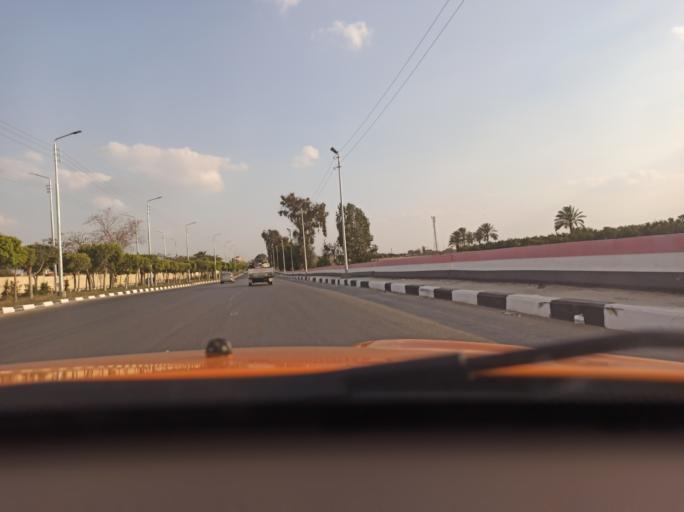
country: EG
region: Al Isma'iliyah
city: Ismailia
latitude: 30.6196
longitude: 32.2470
